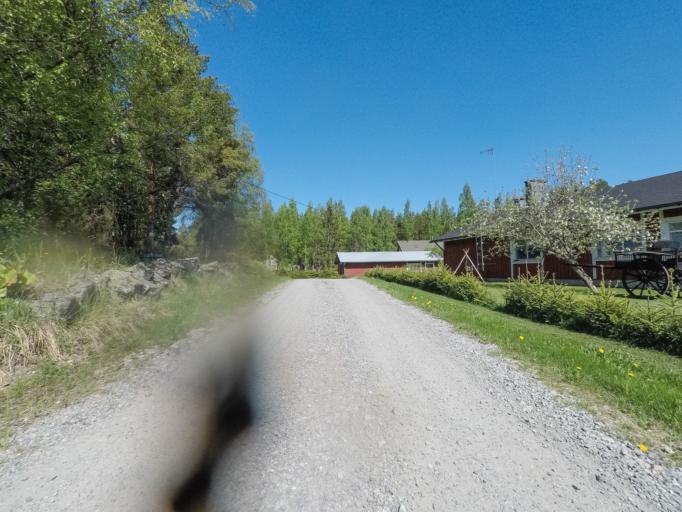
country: FI
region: Pirkanmaa
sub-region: Etelae-Pirkanmaa
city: Kylmaekoski
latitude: 61.1616
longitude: 23.7106
